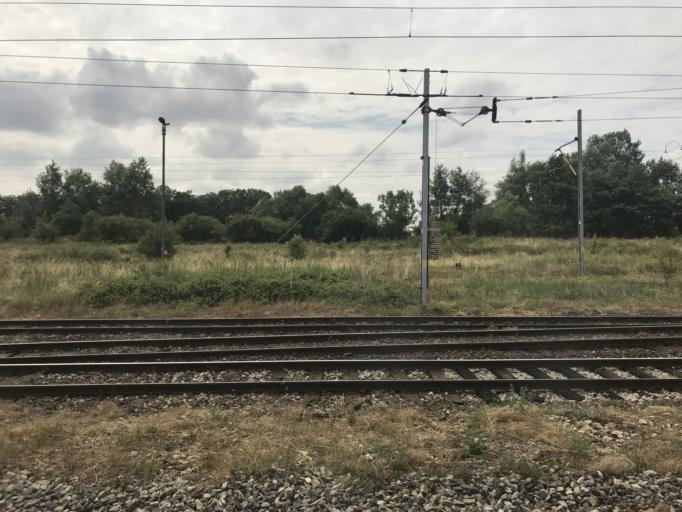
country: PL
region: Greater Poland Voivodeship
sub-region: Powiat gnieznienski
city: Gniezno
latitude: 52.5320
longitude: 17.6350
